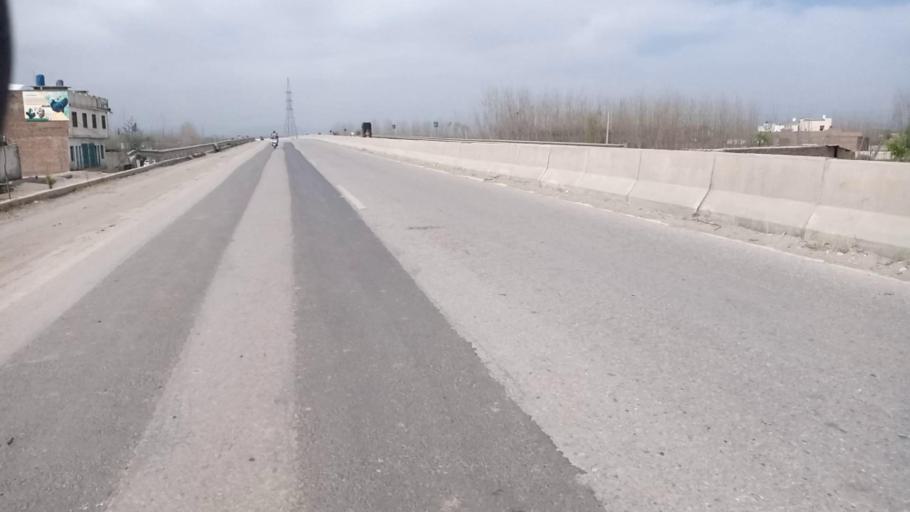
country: PK
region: Khyber Pakhtunkhwa
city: Peshawar
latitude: 34.0531
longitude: 71.6125
